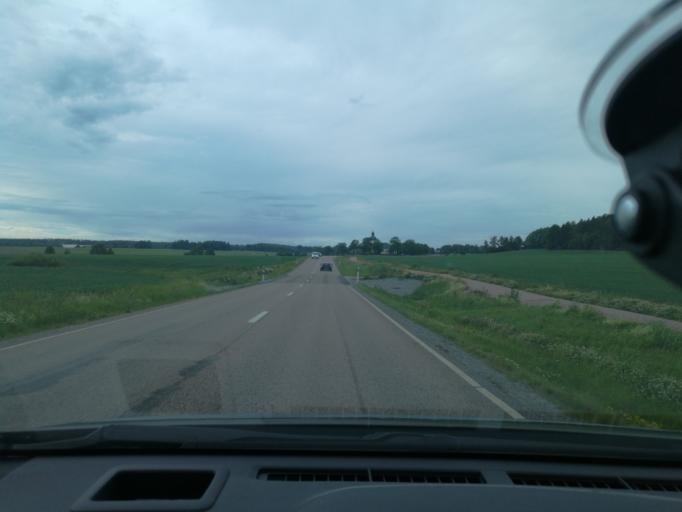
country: SE
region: Vaestmanland
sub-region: Vasteras
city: Skultuna
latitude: 59.6943
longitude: 16.4368
